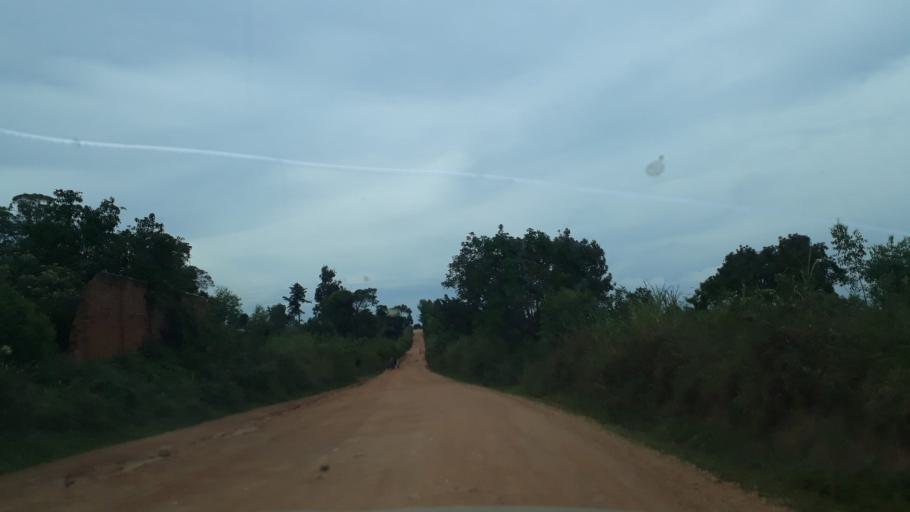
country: UG
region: Northern Region
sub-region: Zombo District
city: Paidha
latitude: 2.0446
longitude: 30.6223
